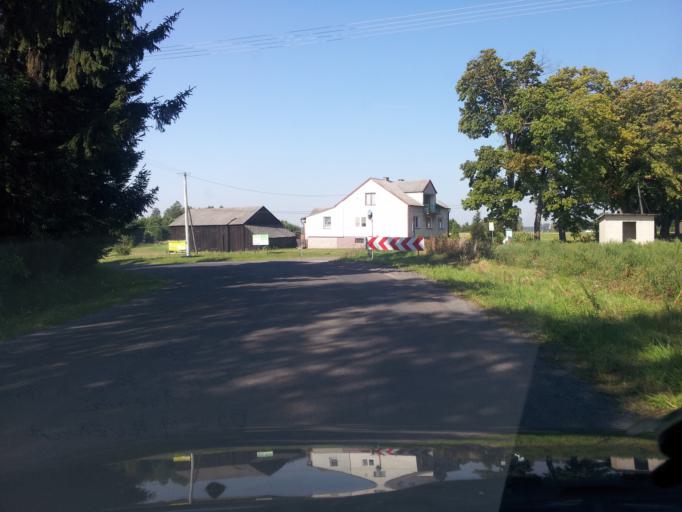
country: PL
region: Kujawsko-Pomorskie
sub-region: Powiat brodnicki
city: Swiedziebnia
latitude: 53.1693
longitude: 19.5900
